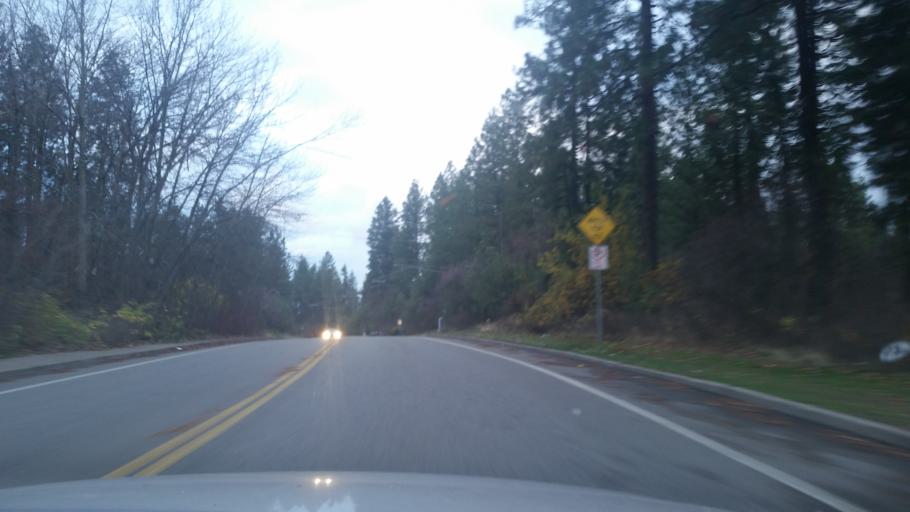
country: US
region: Washington
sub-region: Spokane County
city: Spokane
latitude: 47.6367
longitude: -117.3780
